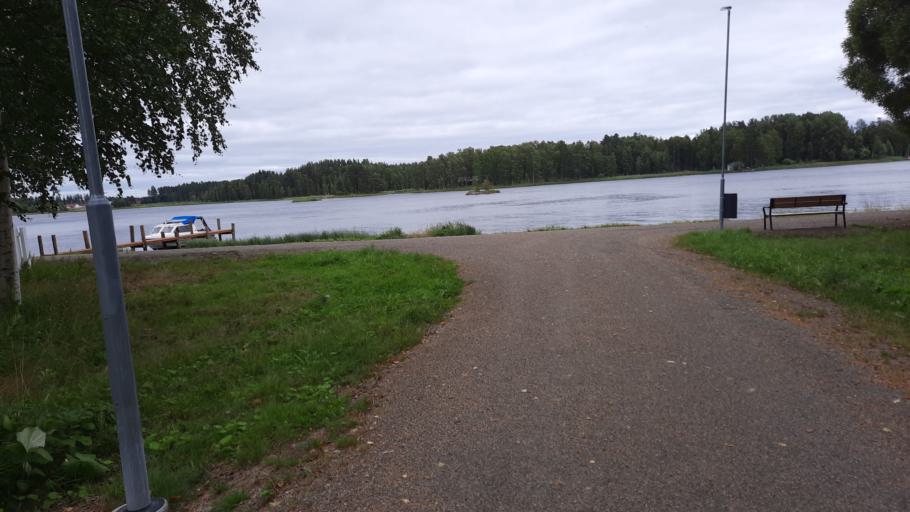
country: FI
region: North Karelia
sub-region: Joensuu
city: Joensuu
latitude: 62.6104
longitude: 29.8349
